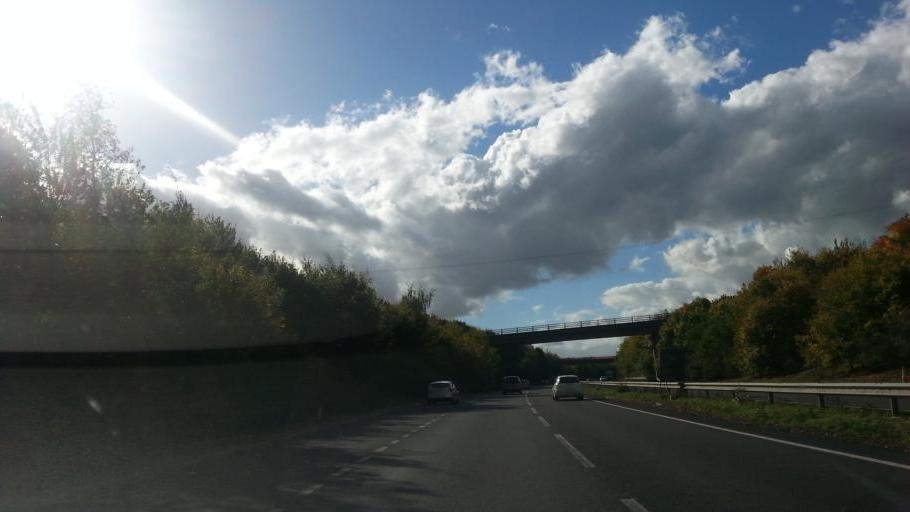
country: GB
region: England
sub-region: Cambridgeshire
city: Comberton
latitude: 52.2181
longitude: 0.0411
